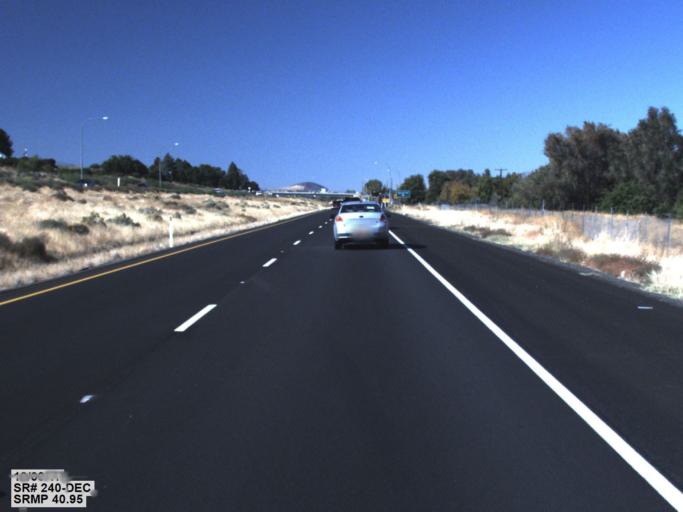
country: US
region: Washington
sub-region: Franklin County
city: West Pasco
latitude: 46.2270
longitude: -119.1816
